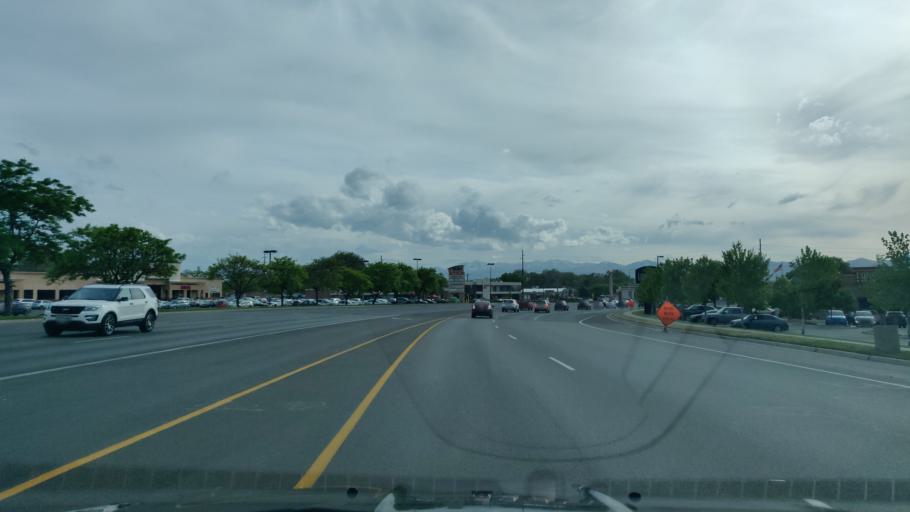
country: US
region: Utah
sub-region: Salt Lake County
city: Sandy City
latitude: 40.6231
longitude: -111.8629
